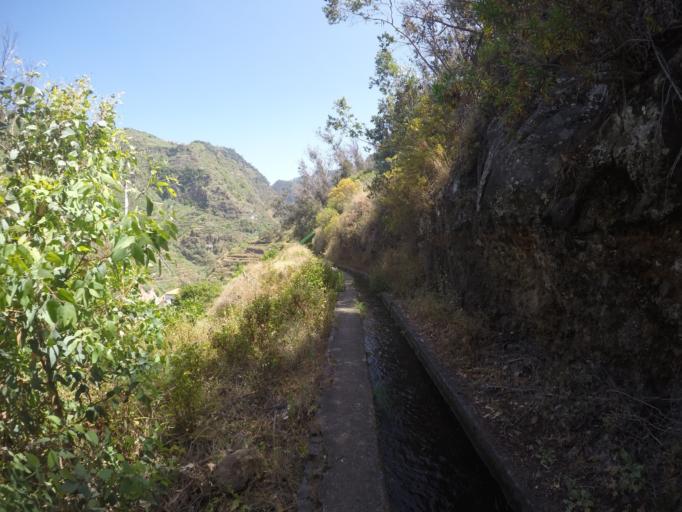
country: PT
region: Madeira
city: Camara de Lobos
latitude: 32.6641
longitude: -16.9590
